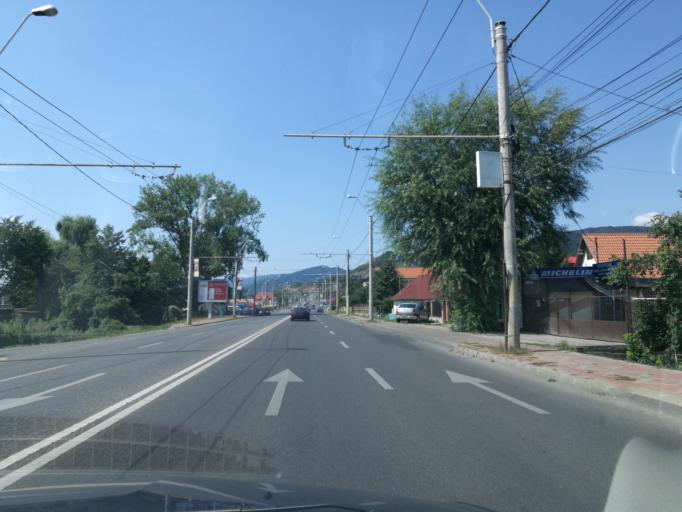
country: RO
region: Neamt
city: Piatra Neamt
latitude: 46.9381
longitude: 26.3414
